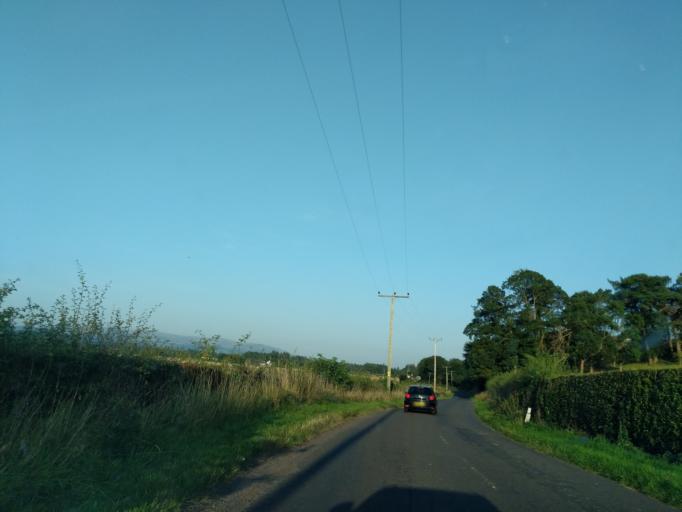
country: GB
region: Scotland
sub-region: Stirling
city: Doune
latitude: 56.1274
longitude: -4.0942
